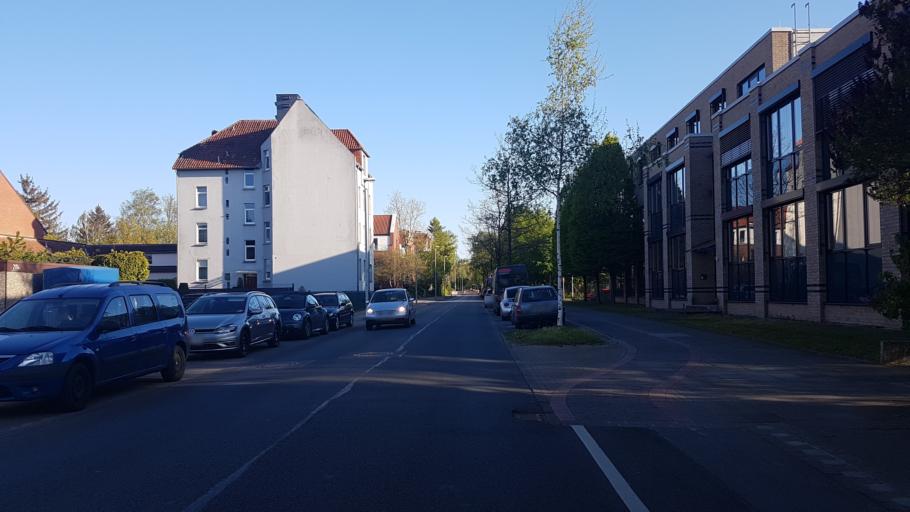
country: DE
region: Lower Saxony
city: Hannover
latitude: 52.3952
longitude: 9.8035
